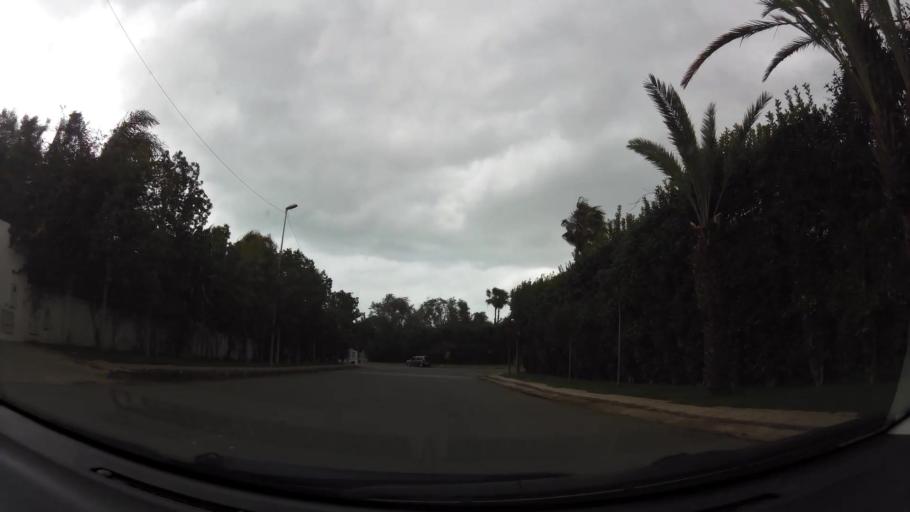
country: MA
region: Grand Casablanca
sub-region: Casablanca
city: Casablanca
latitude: 33.5829
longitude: -7.6729
